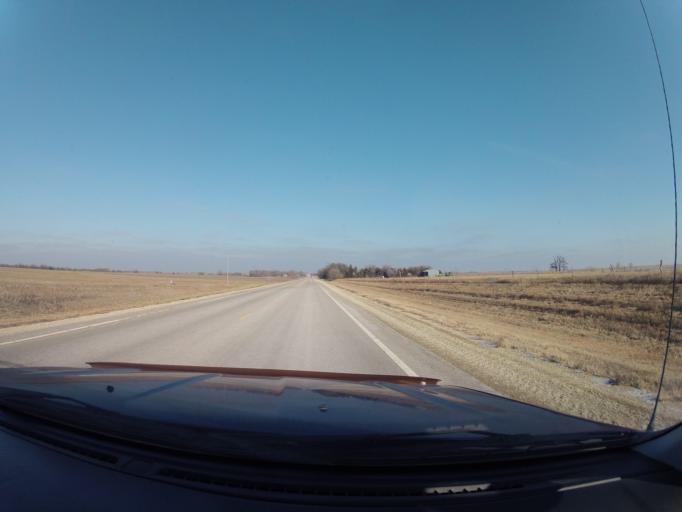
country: US
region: Kansas
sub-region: Marshall County
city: Blue Rapids
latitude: 39.6070
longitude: -96.7501
